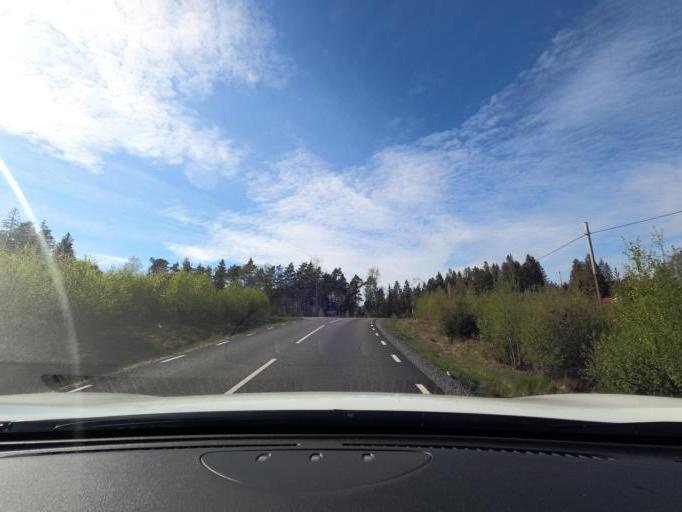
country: SE
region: Vaestra Goetaland
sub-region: Harryda Kommun
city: Landvetter
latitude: 57.6407
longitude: 12.2549
